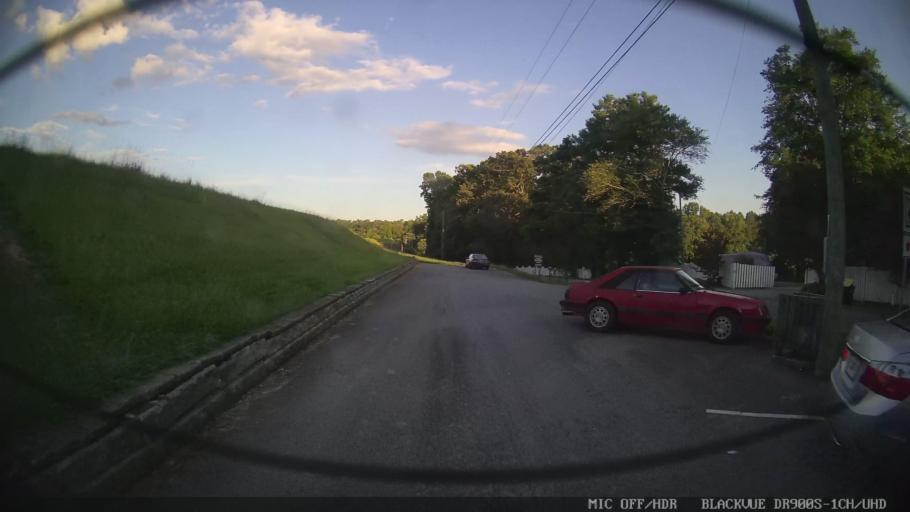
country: US
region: Georgia
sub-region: Bartow County
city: Emerson
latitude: 34.1131
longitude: -84.7139
